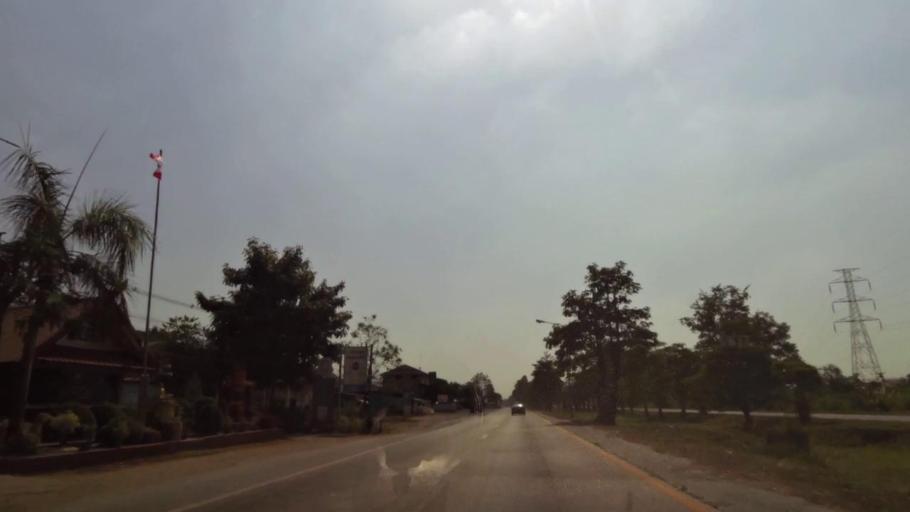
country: TH
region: Phichit
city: Wachira Barami
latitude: 16.5044
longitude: 100.1435
